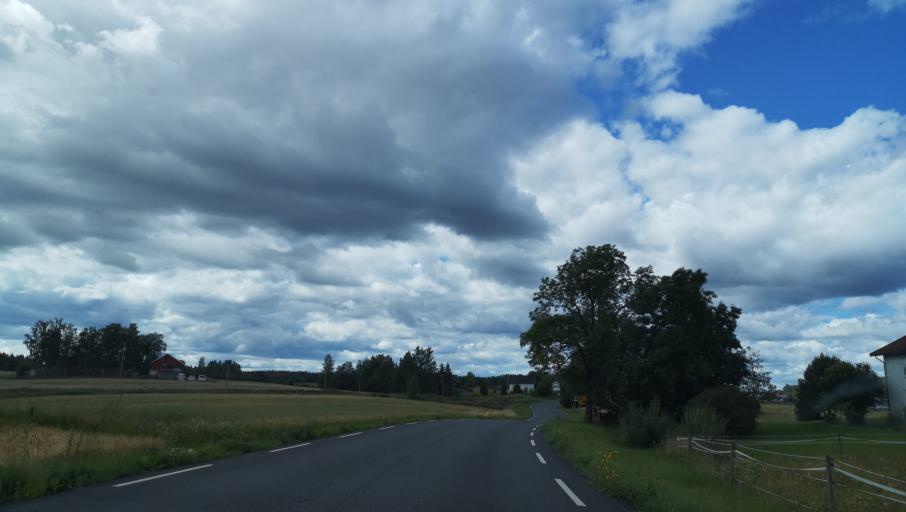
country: NO
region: Akershus
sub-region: Ski
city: Ski
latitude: 59.7091
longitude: 10.8774
